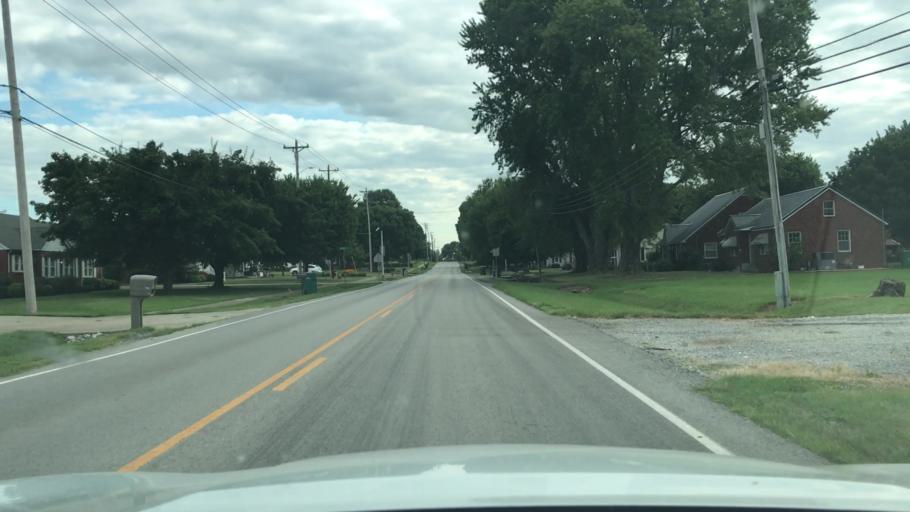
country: US
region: Kentucky
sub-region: Todd County
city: Elkton
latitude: 36.7990
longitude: -87.1589
